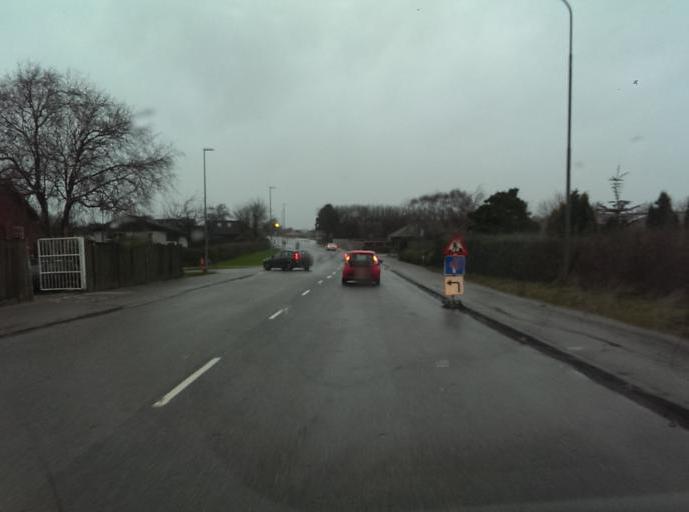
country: DK
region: South Denmark
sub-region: Esbjerg Kommune
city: Esbjerg
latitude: 55.4898
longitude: 8.4592
